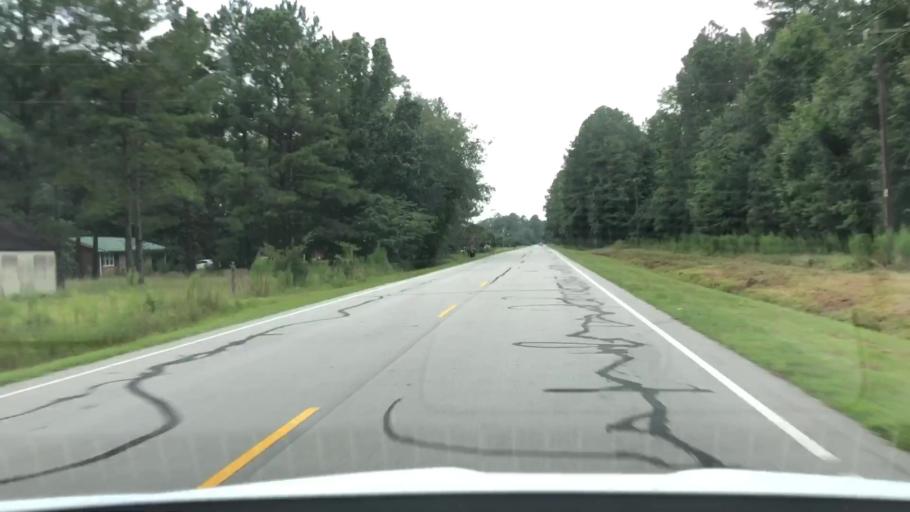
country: US
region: North Carolina
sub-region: Lenoir County
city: Kinston
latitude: 35.1158
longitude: -77.5118
